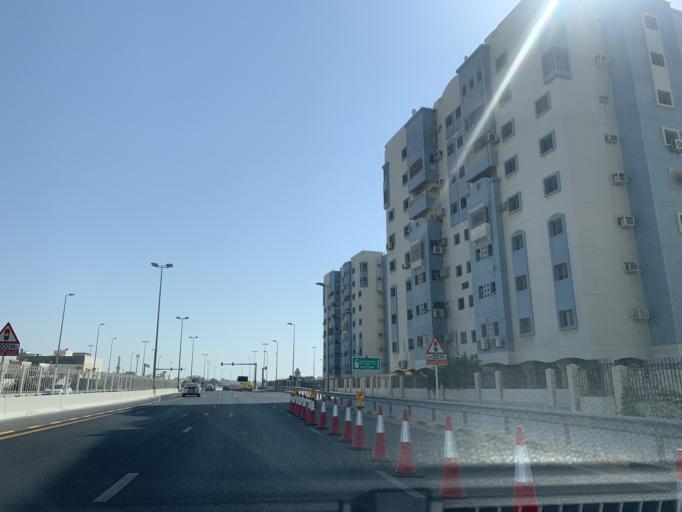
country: BH
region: Central Governorate
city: Madinat Hamad
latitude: 26.1148
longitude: 50.4916
